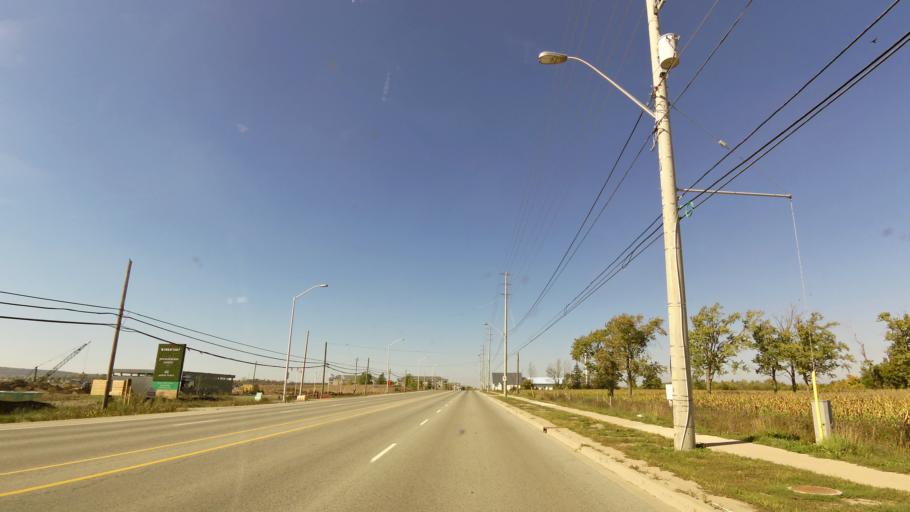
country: CA
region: Ontario
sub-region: Halton
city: Milton
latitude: 43.4931
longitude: -79.8435
